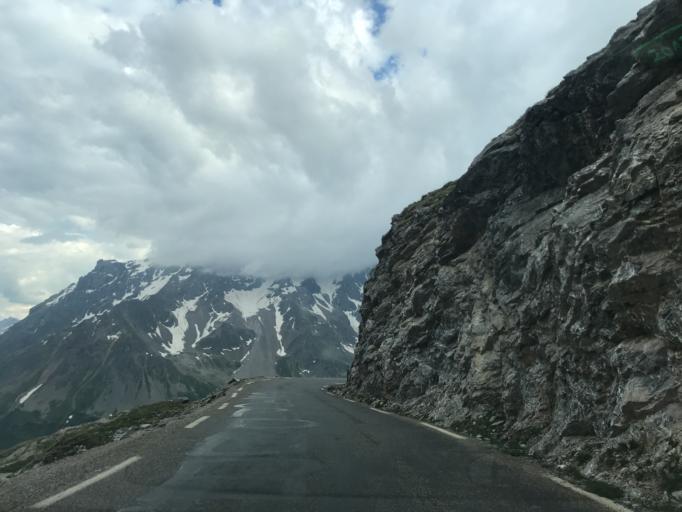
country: FR
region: Rhone-Alpes
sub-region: Departement de la Savoie
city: Valloire
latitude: 45.0567
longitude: 6.4084
